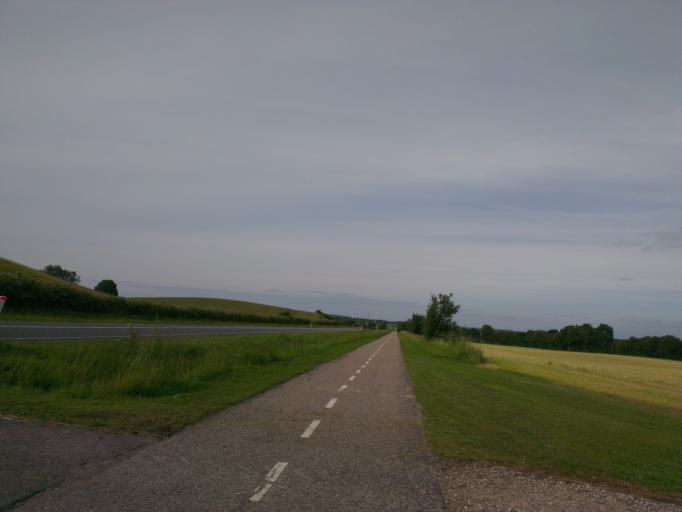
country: DK
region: Capital Region
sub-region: Frederikssund Kommune
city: Skibby
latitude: 55.7785
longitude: 11.9654
